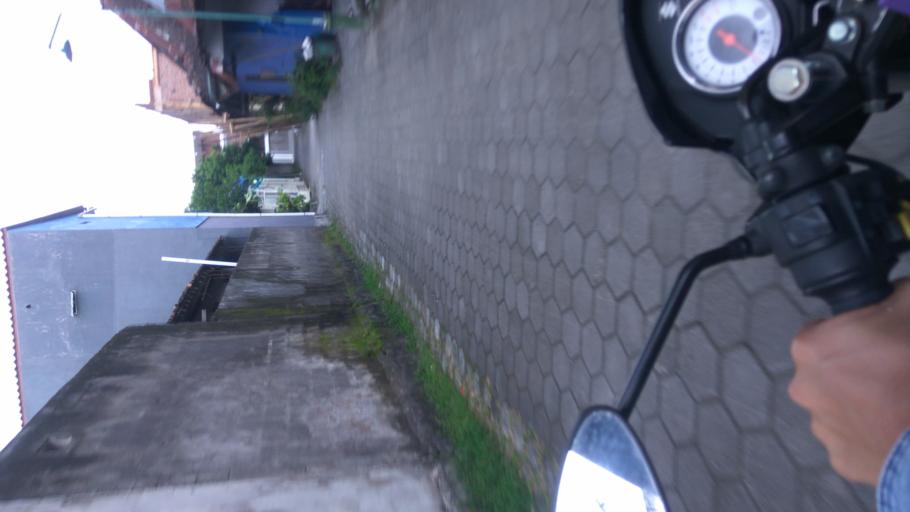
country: ID
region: Daerah Istimewa Yogyakarta
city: Depok
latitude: -7.7574
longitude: 110.4132
